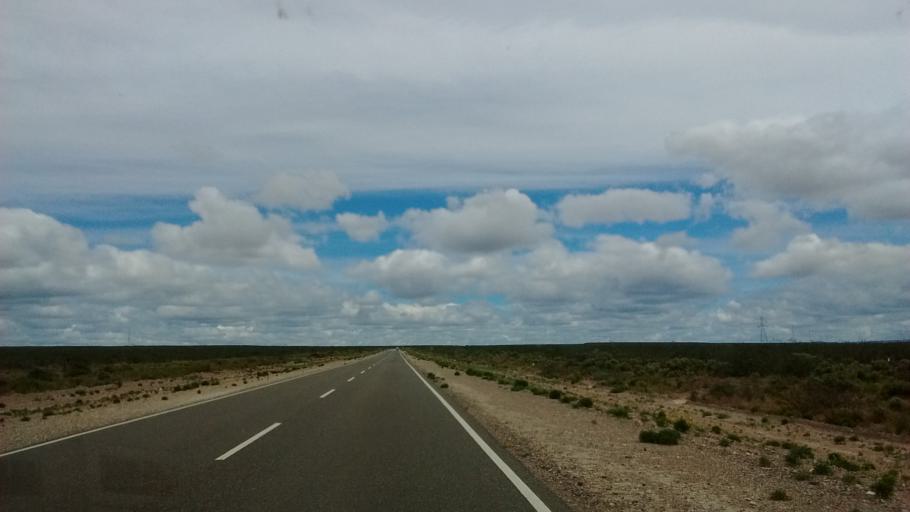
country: AR
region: Neuquen
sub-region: Departamento de Picun Leufu
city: Picun Leufu
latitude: -39.7438
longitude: -69.6082
